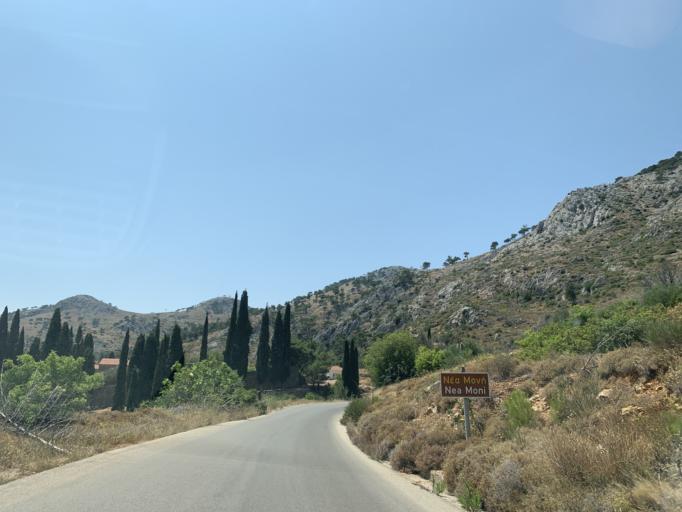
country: GR
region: North Aegean
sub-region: Chios
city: Chios
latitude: 38.3758
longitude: 26.0556
